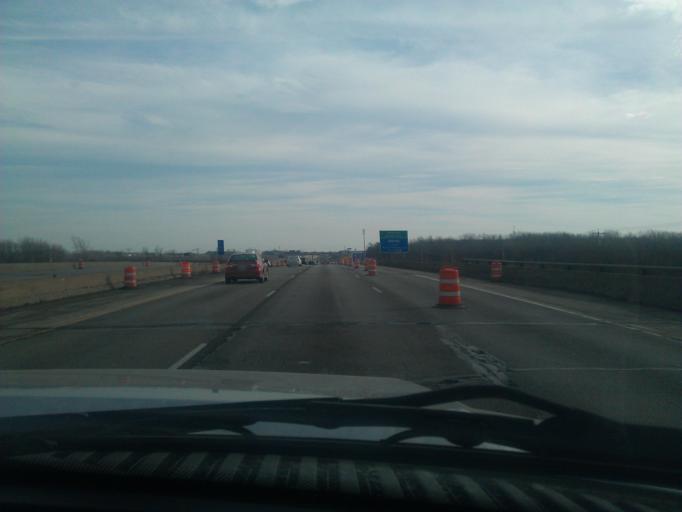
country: US
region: Wisconsin
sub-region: Racine County
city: Franksville
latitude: 42.7429
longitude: -87.9542
